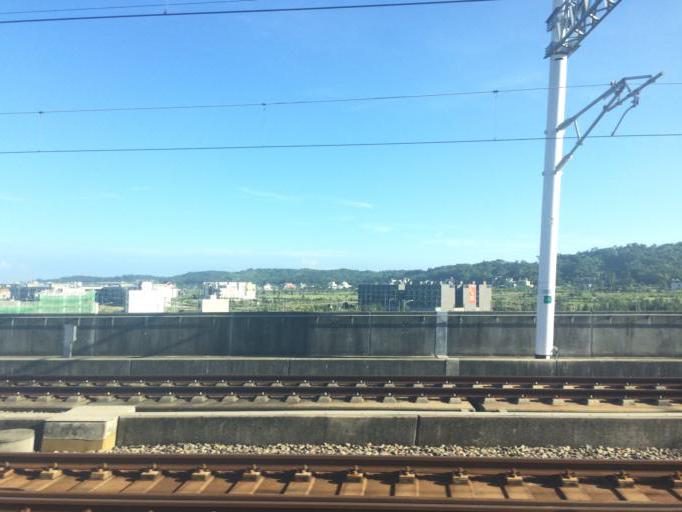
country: TW
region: Taiwan
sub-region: Miaoli
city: Miaoli
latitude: 24.6080
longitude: 120.8314
